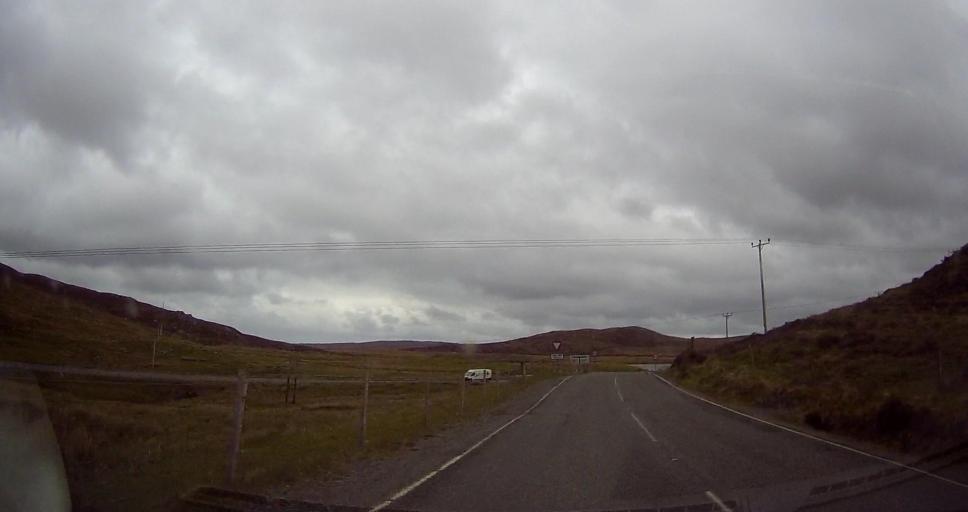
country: GB
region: Scotland
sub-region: Shetland Islands
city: Lerwick
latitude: 60.3494
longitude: -1.2564
